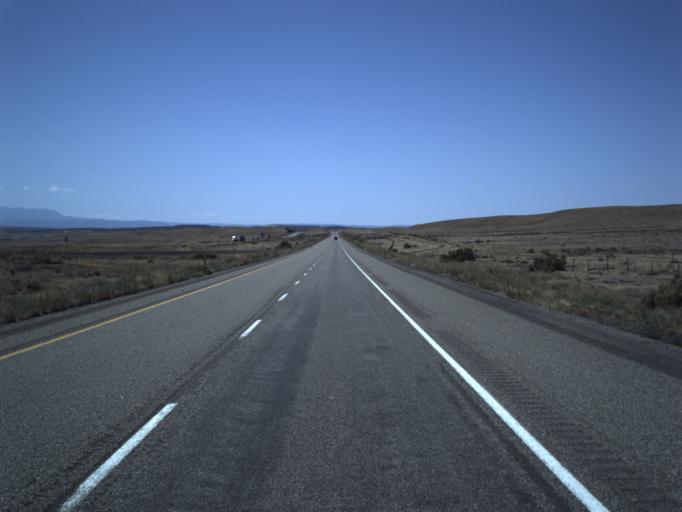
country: US
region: Colorado
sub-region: Mesa County
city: Loma
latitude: 39.1583
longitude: -109.1438
